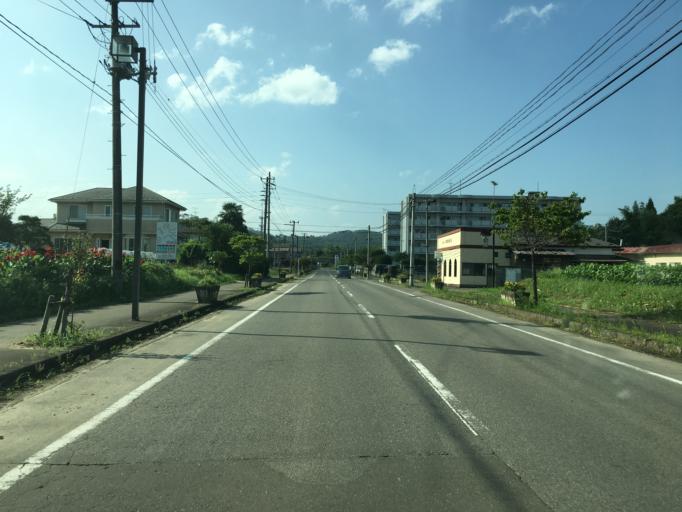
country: JP
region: Miyagi
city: Marumori
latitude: 37.9281
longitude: 140.7636
